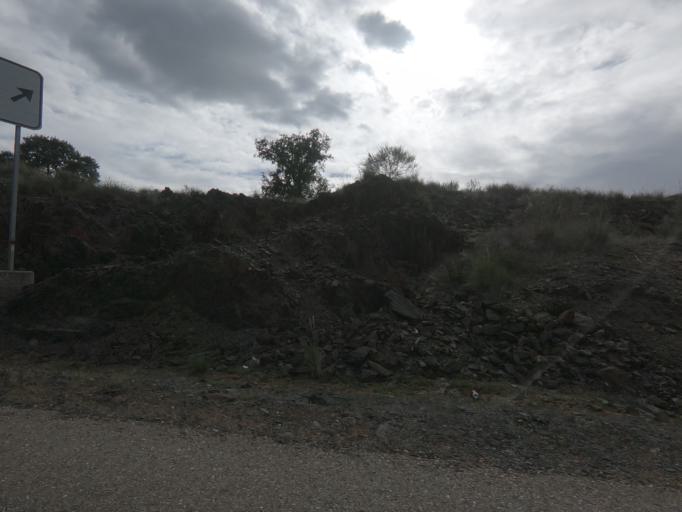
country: ES
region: Castille and Leon
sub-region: Provincia de Salamanca
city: Herguijuela de Ciudad Rodrigo
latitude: 40.4850
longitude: -6.5821
